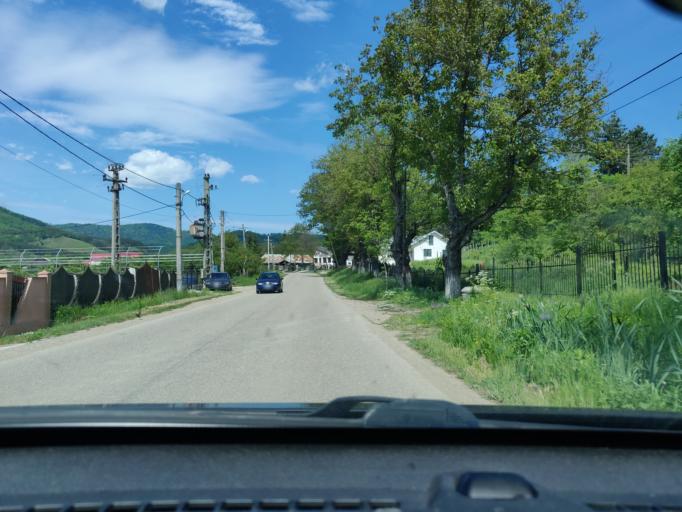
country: RO
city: Vizantea-Manastireasca
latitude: 45.9815
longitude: 26.7956
